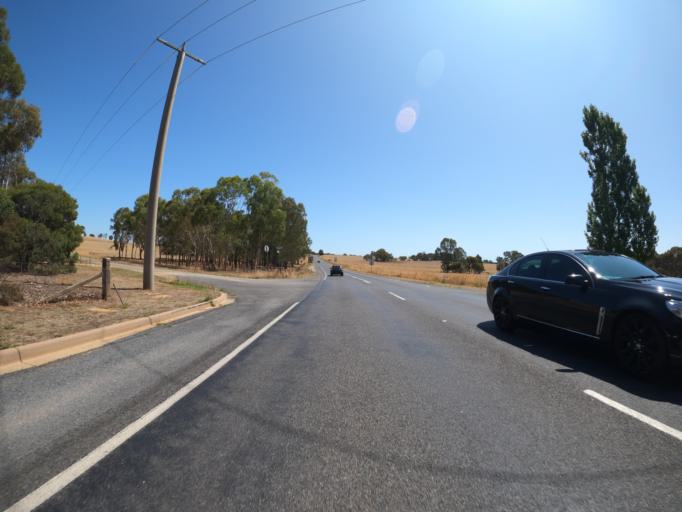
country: AU
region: New South Wales
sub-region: Corowa Shire
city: Corowa
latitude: -36.0536
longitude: 146.4481
